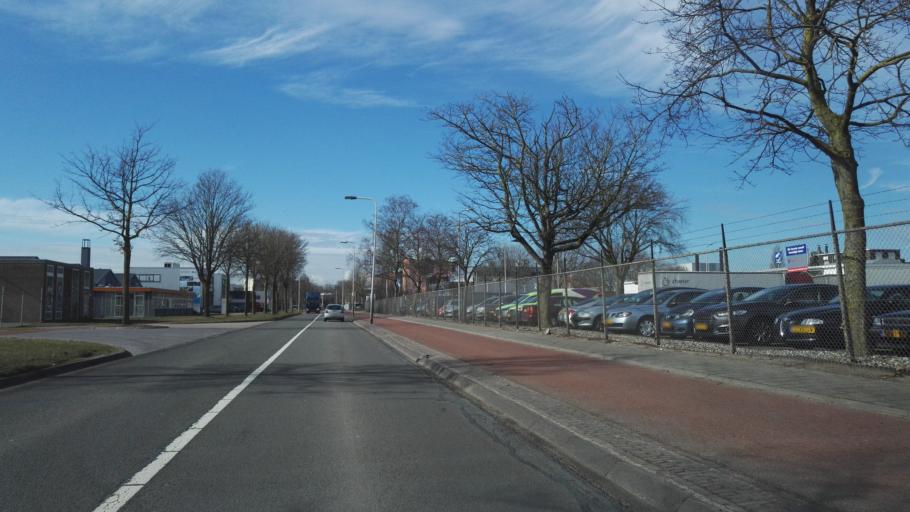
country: NL
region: Overijssel
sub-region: Gemeente Deventer
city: Deventer
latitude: 52.2431
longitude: 6.1838
